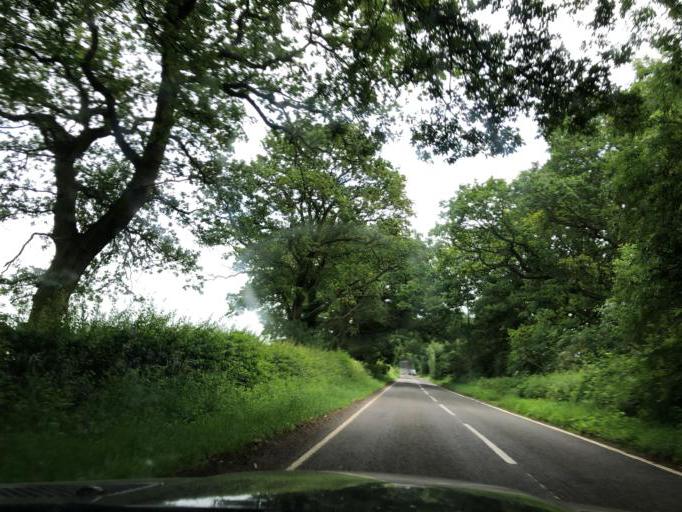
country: GB
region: England
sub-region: Warwickshire
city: Kenilworth
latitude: 52.3259
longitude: -1.6069
